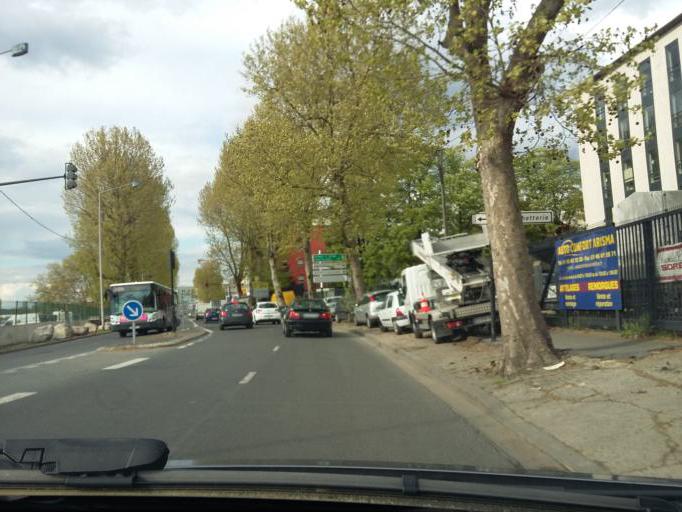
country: FR
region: Ile-de-France
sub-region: Departement de Seine-Saint-Denis
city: Saint-Denis
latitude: 48.9313
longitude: 2.3417
